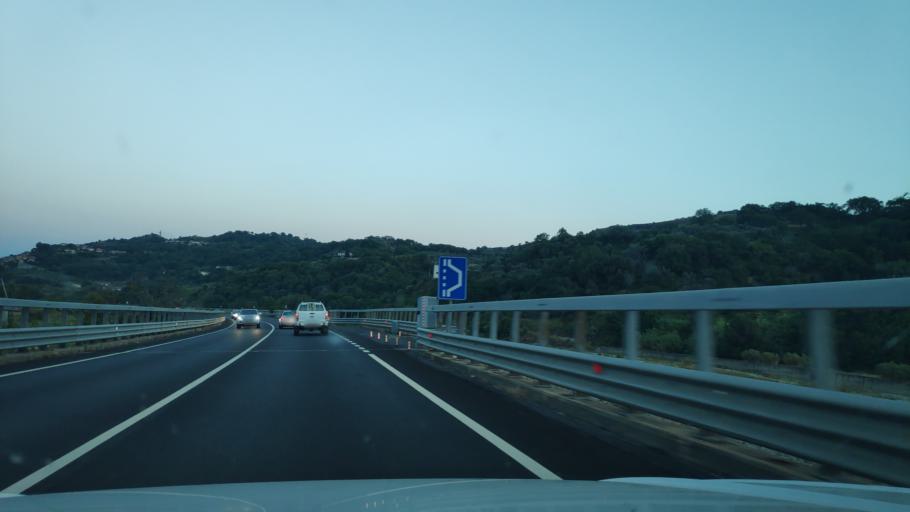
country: IT
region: Calabria
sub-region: Provincia di Reggio Calabria
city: Grotteria
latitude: 38.3470
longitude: 16.2568
